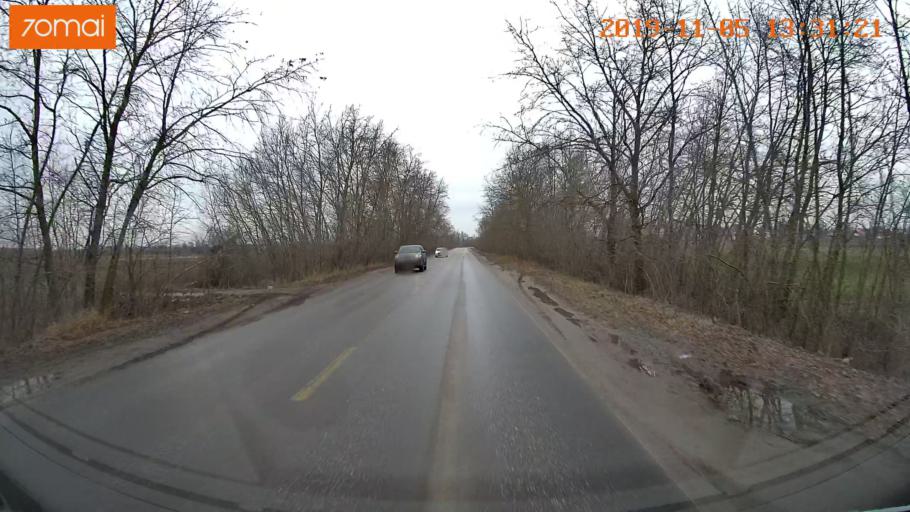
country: RU
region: Ivanovo
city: Shuya
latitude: 56.8748
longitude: 41.3930
